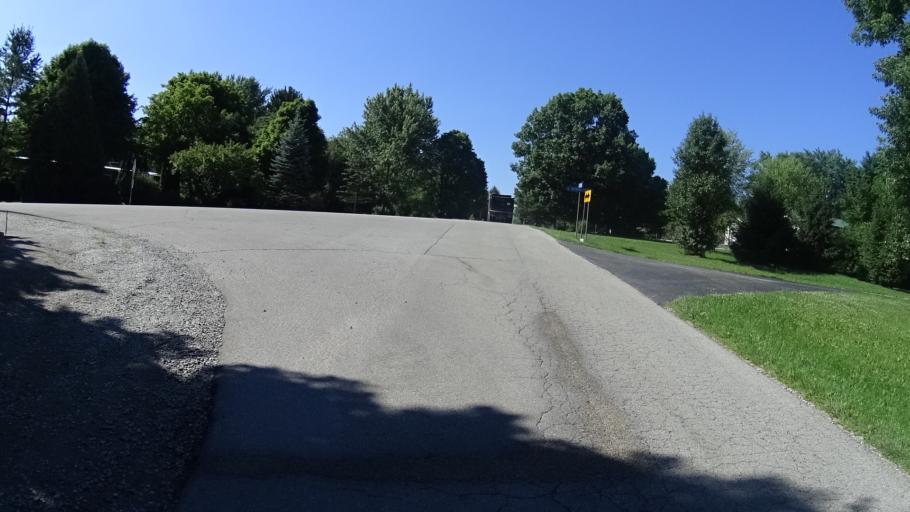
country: US
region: Indiana
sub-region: Madison County
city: Ingalls
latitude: 39.9597
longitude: -85.8150
